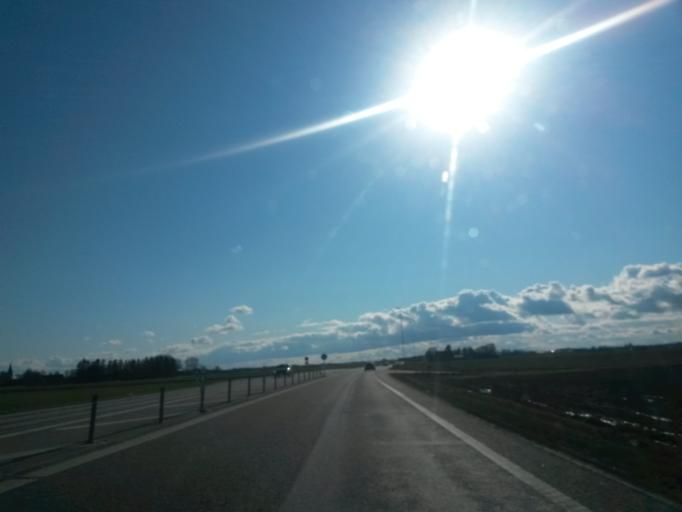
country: SE
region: Vaestra Goetaland
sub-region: Vara Kommun
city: Vara
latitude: 58.2714
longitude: 13.0105
